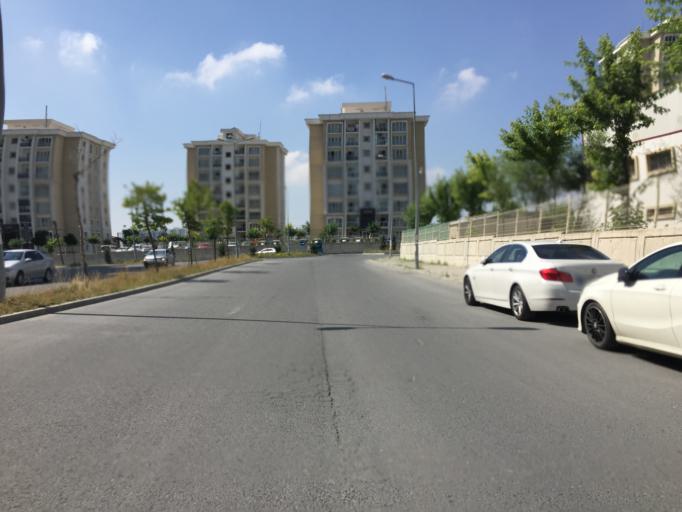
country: TR
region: Istanbul
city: Esenyurt
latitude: 41.0843
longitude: 28.6552
